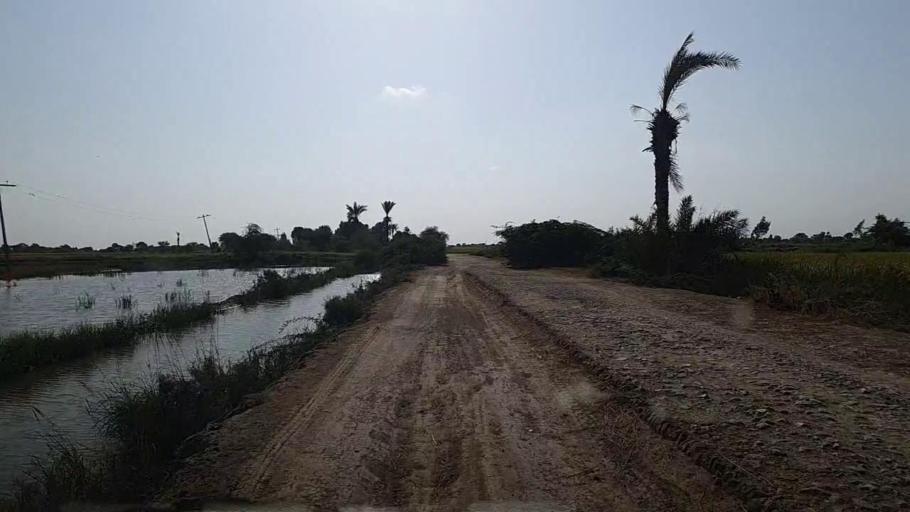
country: PK
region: Sindh
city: Kario
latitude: 24.8050
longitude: 68.5131
